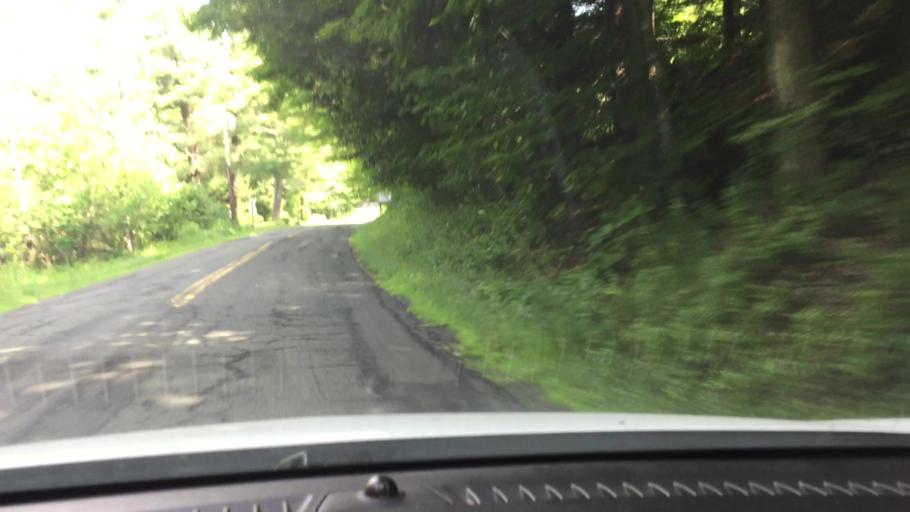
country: US
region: Massachusetts
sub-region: Berkshire County
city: Otis
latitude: 42.1965
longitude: -73.1618
